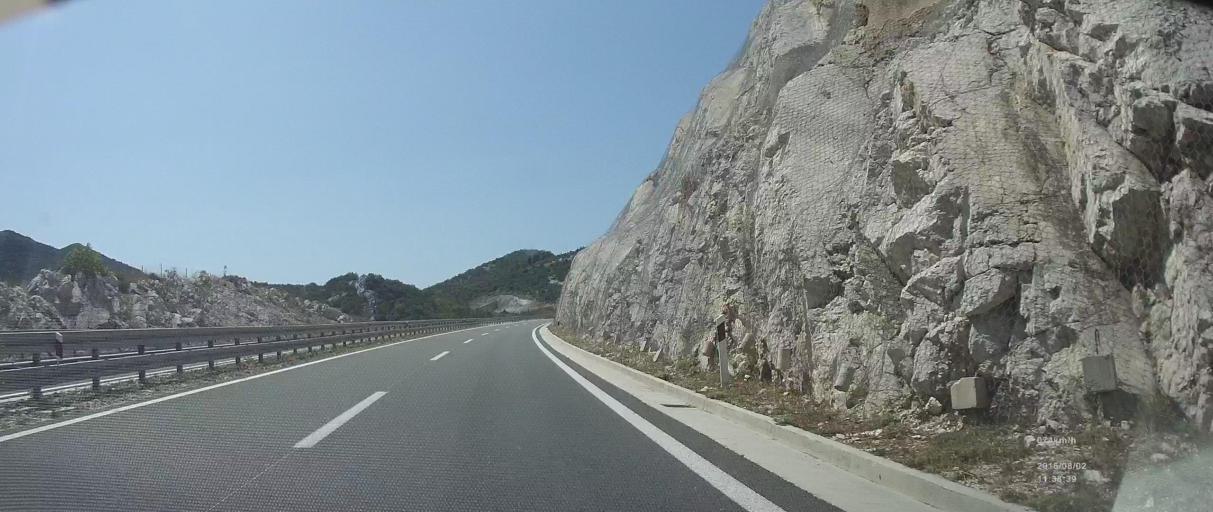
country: HR
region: Dubrovacko-Neretvanska
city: Komin
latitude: 43.0937
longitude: 17.4908
